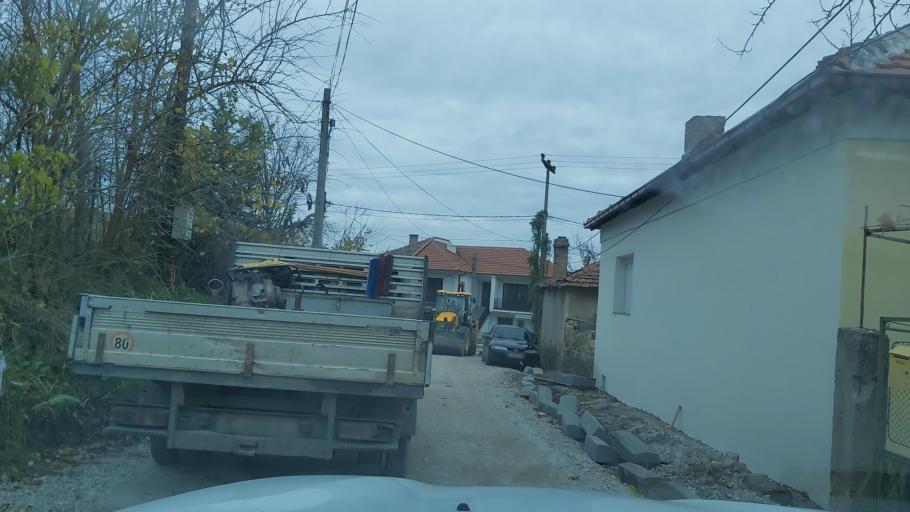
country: MK
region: Demir Kapija
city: Demir Kapija
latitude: 41.4098
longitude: 22.2374
